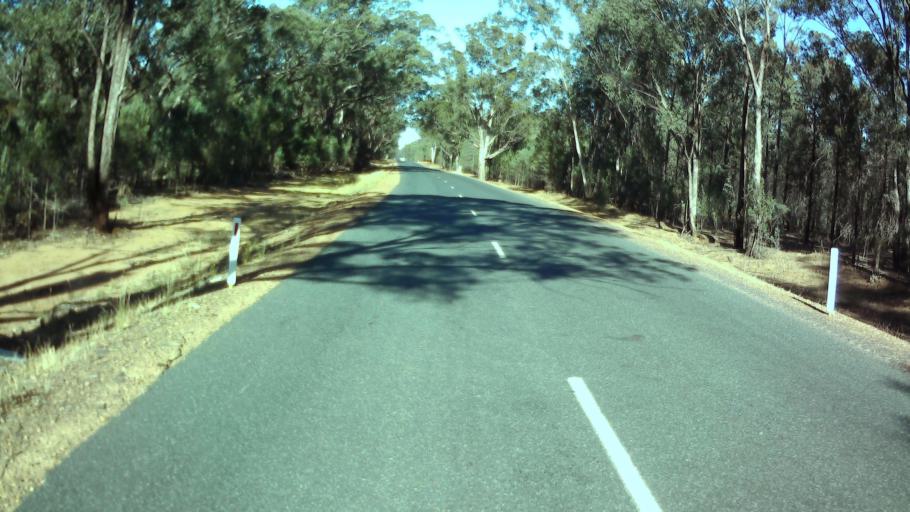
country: AU
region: New South Wales
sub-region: Weddin
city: Grenfell
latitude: -34.0239
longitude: 148.0245
